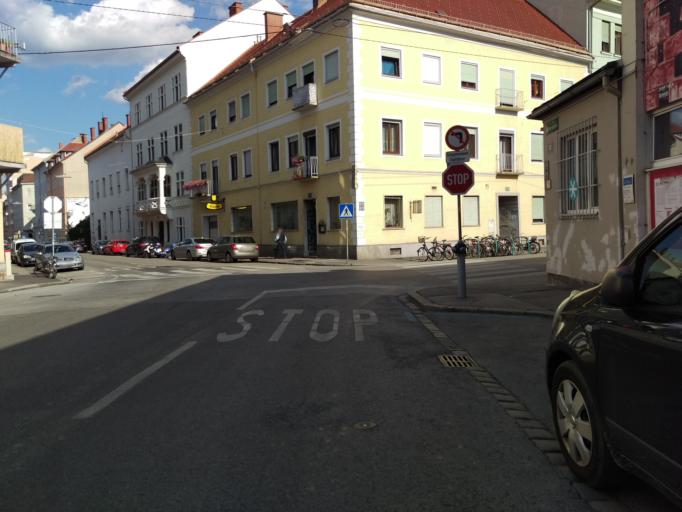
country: AT
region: Styria
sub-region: Graz Stadt
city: Graz
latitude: 47.0672
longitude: 15.4233
